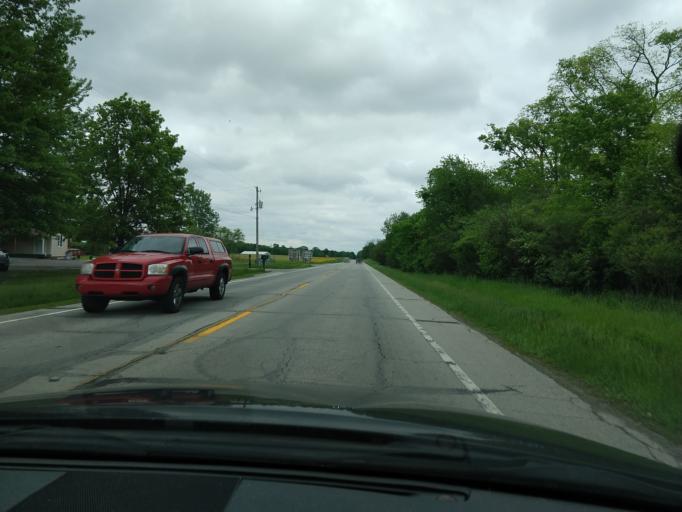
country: US
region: Indiana
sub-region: Hamilton County
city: Noblesville
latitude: 40.0465
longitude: -85.9574
